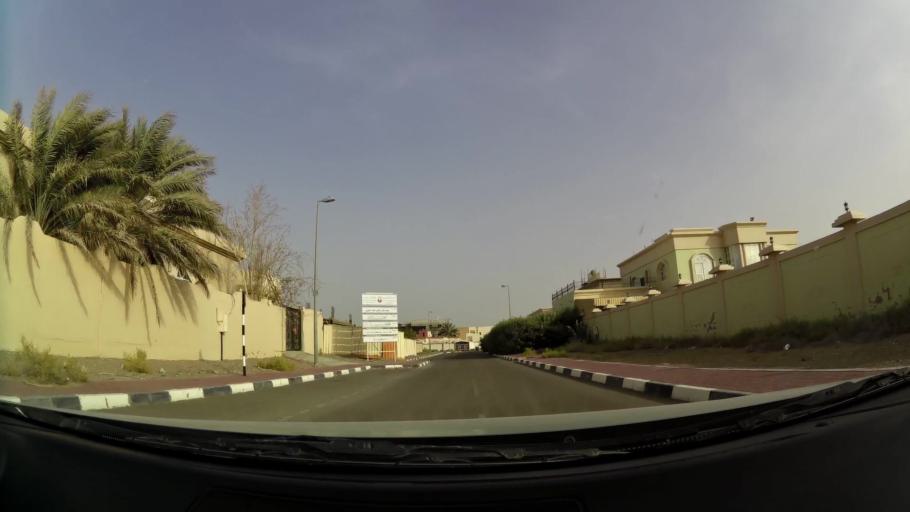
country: AE
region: Abu Dhabi
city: Al Ain
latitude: 24.2188
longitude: 55.6661
